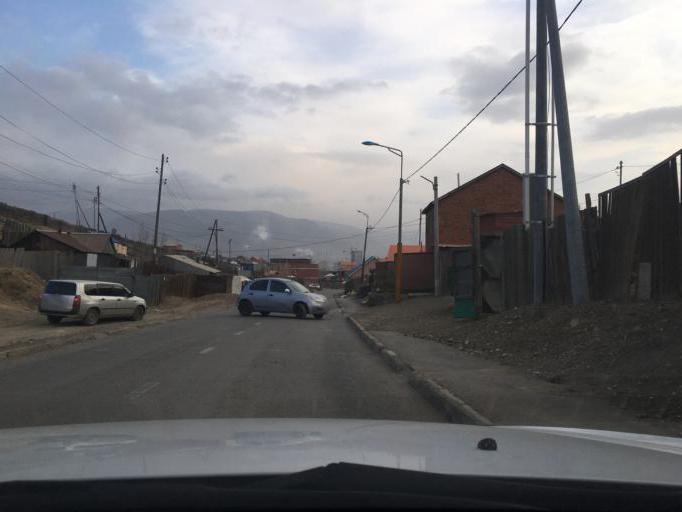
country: MN
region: Ulaanbaatar
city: Ulaanbaatar
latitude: 47.9320
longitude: 106.8582
